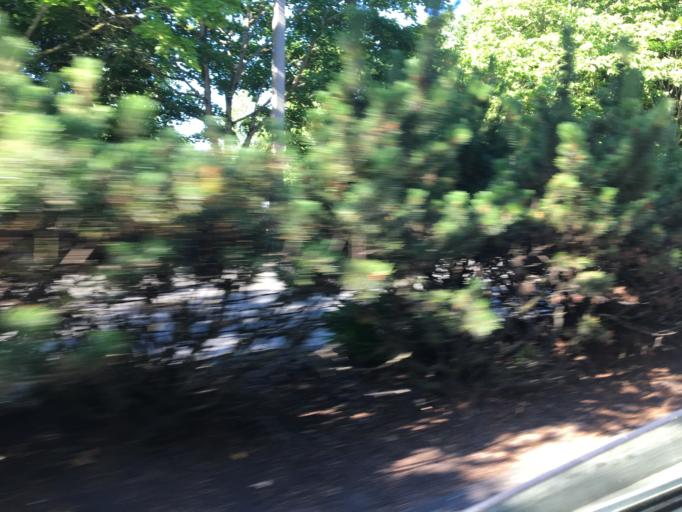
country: US
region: Washington
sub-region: King County
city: Bellevue
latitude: 47.6139
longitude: -122.2051
